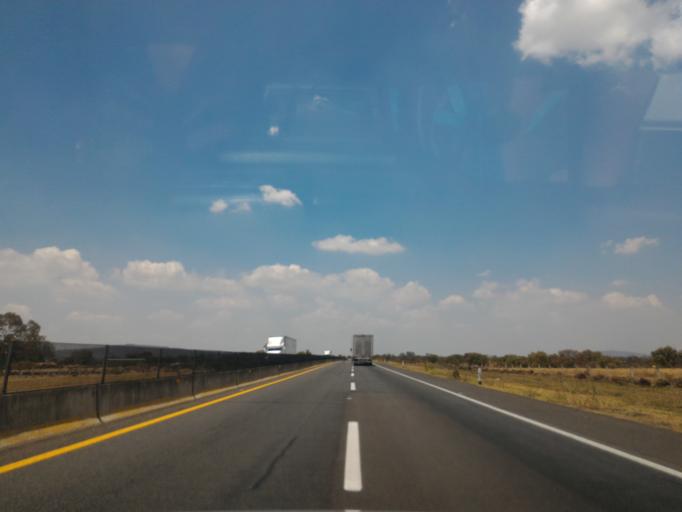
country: MX
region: Jalisco
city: Tepatitlan de Morelos
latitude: 20.8588
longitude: -102.7664
